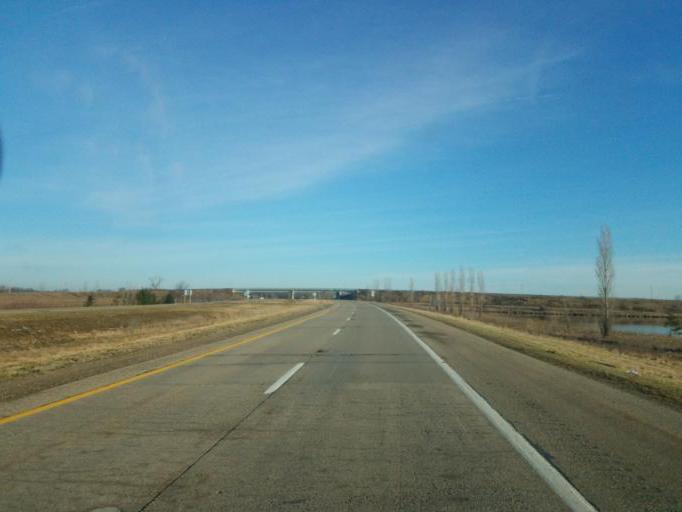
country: US
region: Michigan
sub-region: Clinton County
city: Saint Johns
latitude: 43.0126
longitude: -84.5192
